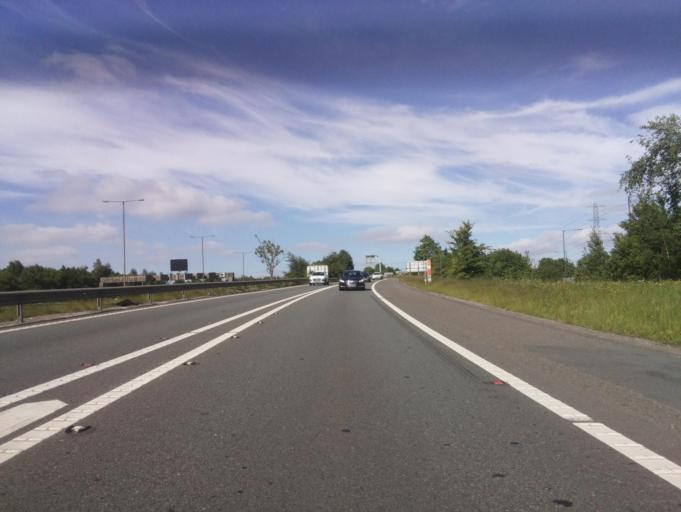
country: GB
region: England
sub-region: Borough of Bolton
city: Kearsley
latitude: 53.5210
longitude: -2.3647
